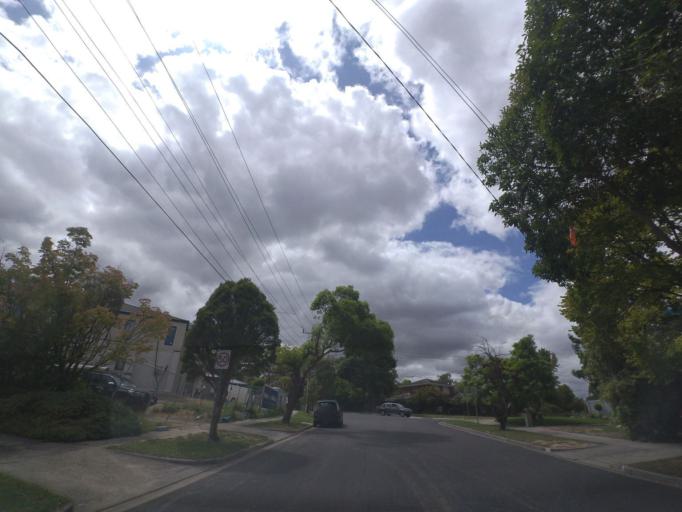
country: AU
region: Victoria
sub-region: Manningham
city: Park Orchards
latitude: -37.7909
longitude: 145.2293
